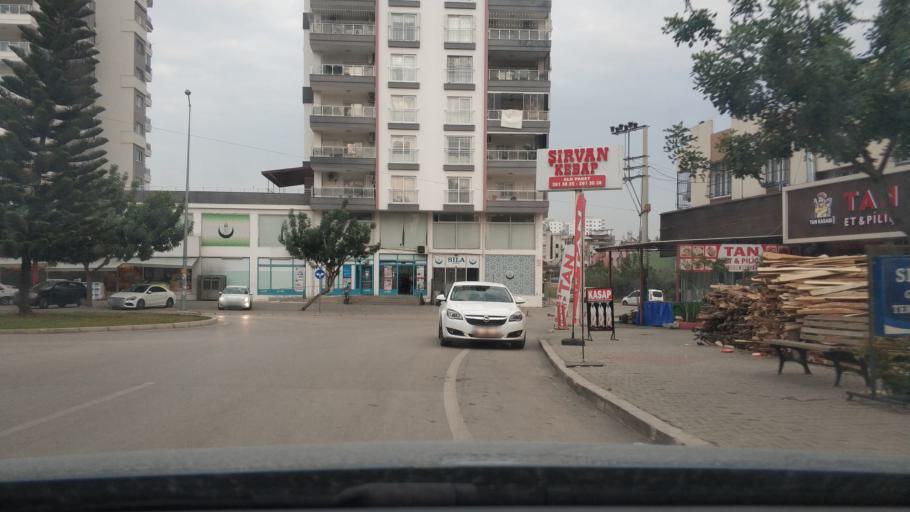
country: TR
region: Adana
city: Seyhan
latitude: 37.0179
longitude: 35.2900
